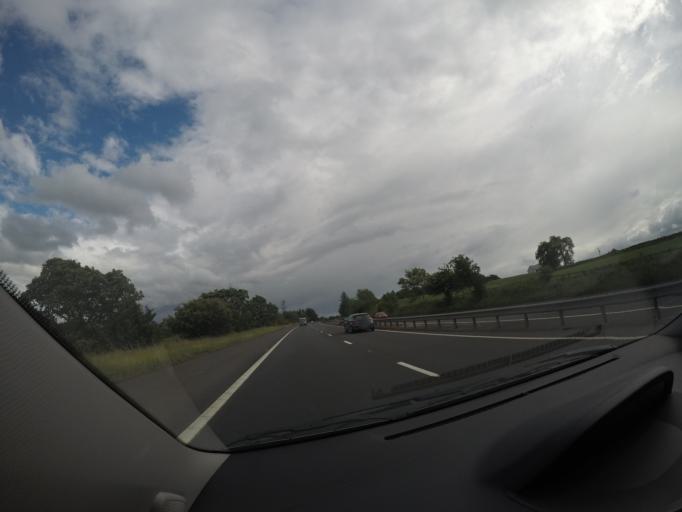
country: GB
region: Scotland
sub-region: Stirling
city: Bannockburn
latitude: 56.0768
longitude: -3.9271
